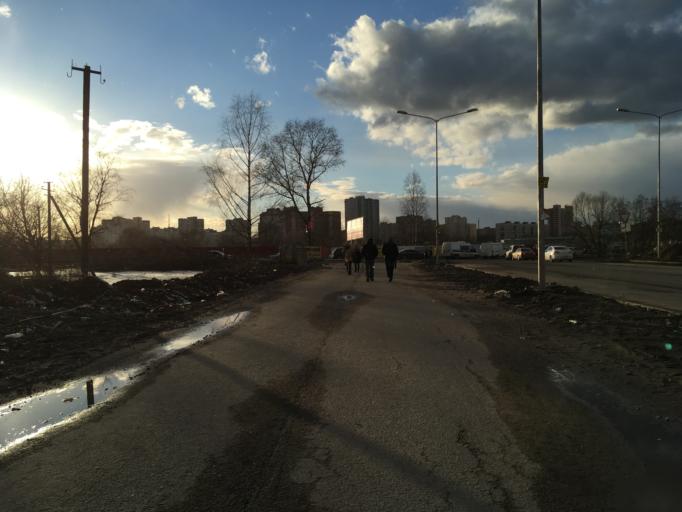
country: RU
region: Leningrad
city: Rybatskoye
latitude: 59.9095
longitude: 30.5092
